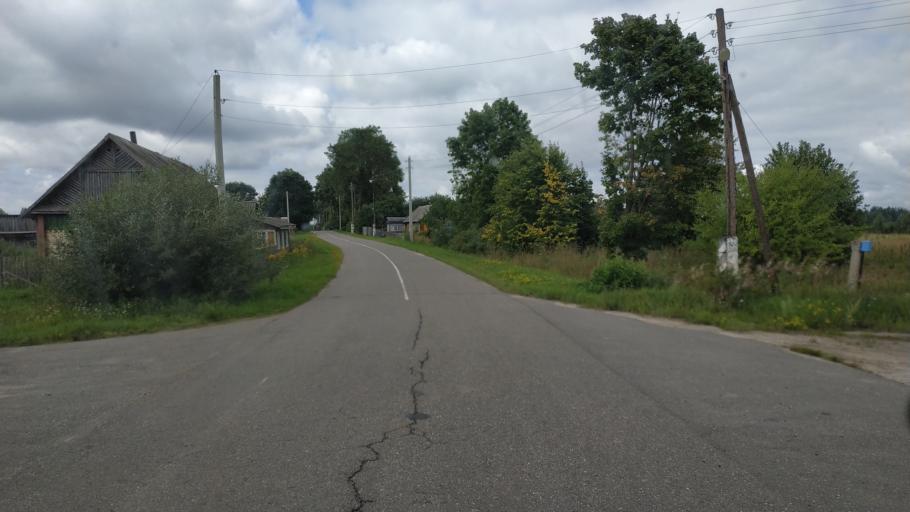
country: BY
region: Mogilev
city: Chavusy
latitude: 53.7805
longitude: 30.8886
